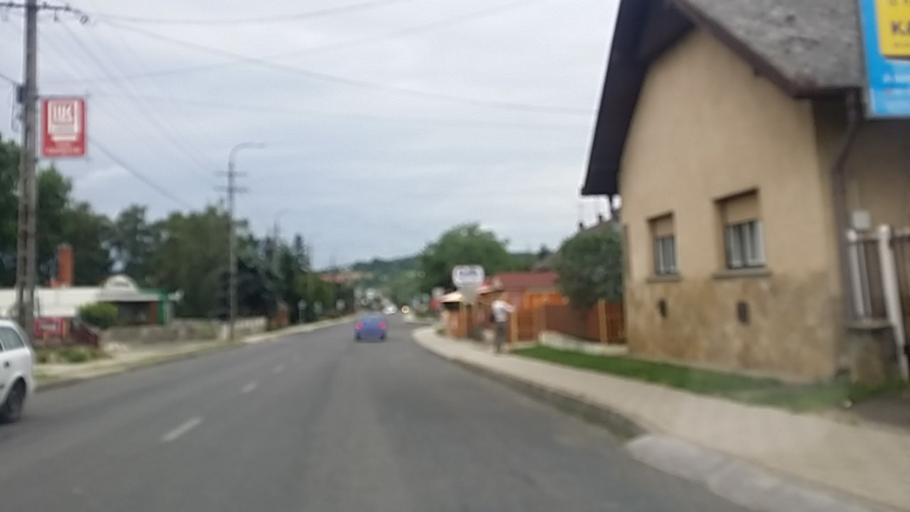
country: HU
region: Zala
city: Zalaegerszeg
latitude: 46.8631
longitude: 16.8002
